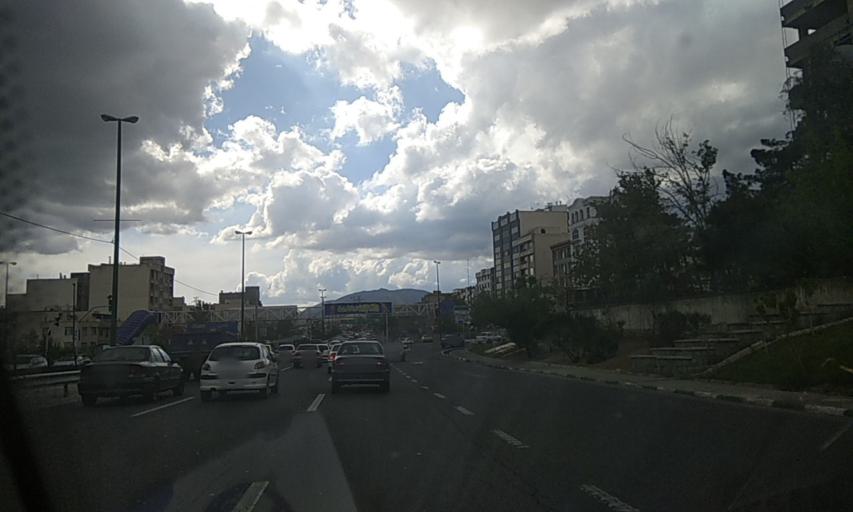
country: IR
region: Tehran
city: Tajrish
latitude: 35.7696
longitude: 51.3288
